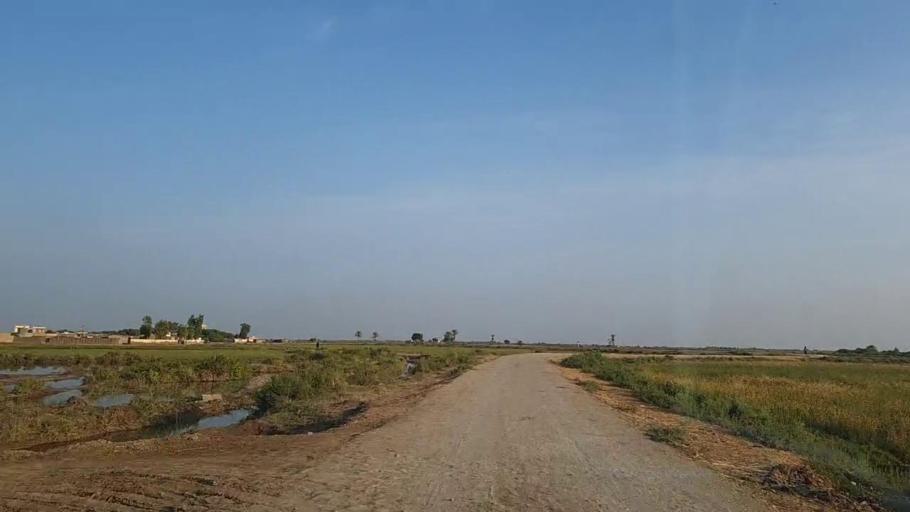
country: PK
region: Sindh
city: Mirpur Batoro
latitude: 24.6086
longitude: 68.0943
